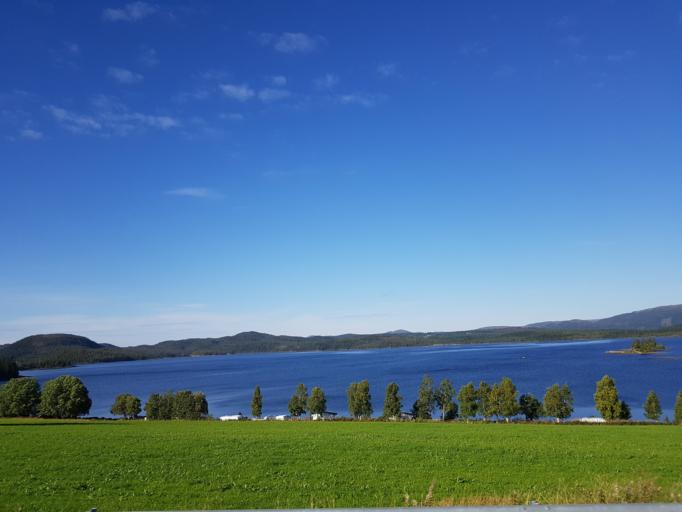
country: NO
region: Sor-Trondelag
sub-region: Trondheim
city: Trondheim
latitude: 63.6168
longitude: 10.2333
